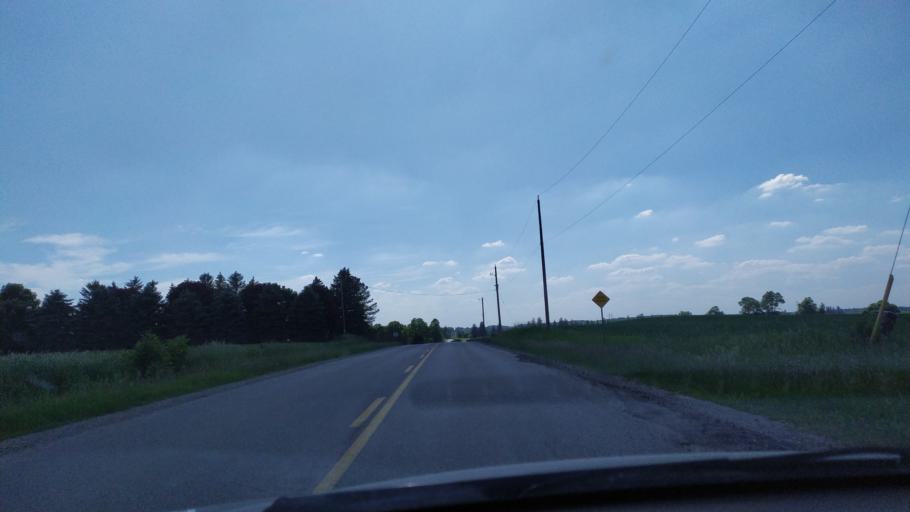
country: CA
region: Ontario
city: Kitchener
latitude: 43.3755
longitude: -80.5294
